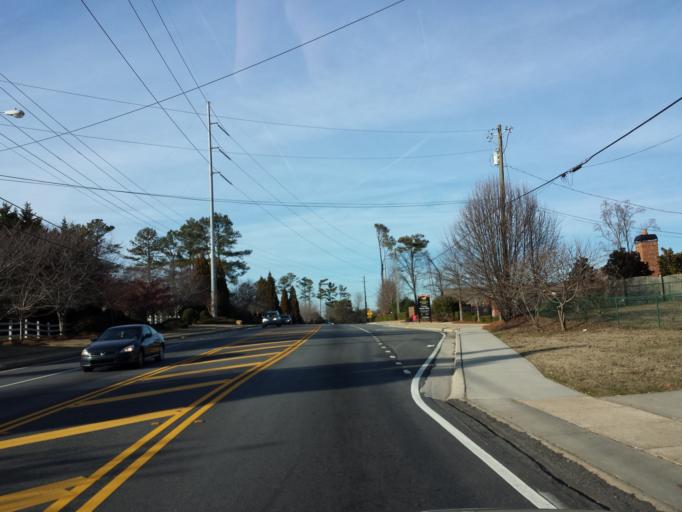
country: US
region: Georgia
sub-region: Cobb County
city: Marietta
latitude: 34.0105
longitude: -84.5478
